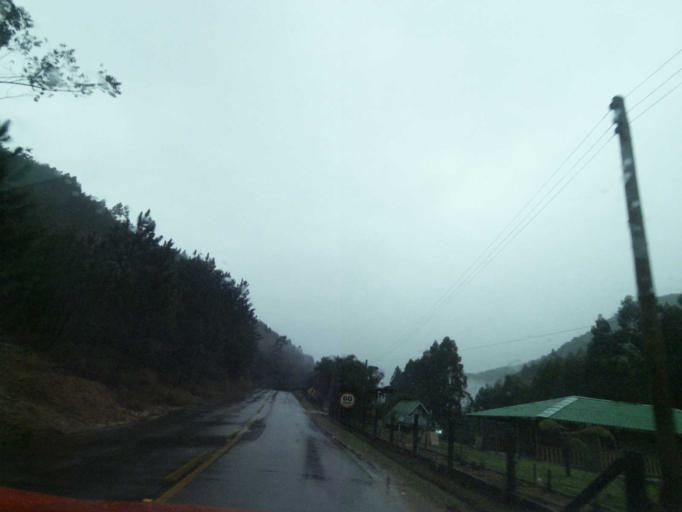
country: BR
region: Santa Catarina
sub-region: Anitapolis
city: Anitapolis
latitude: -27.8278
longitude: -49.0506
